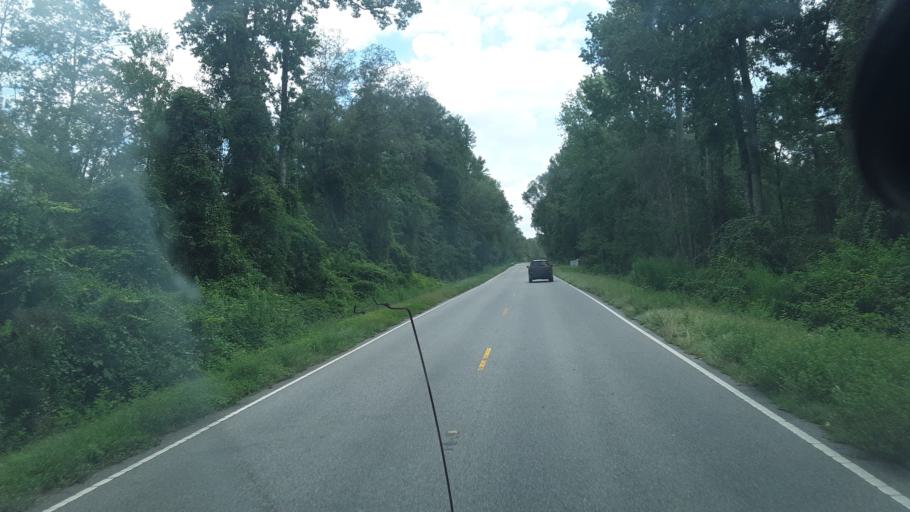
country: US
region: North Carolina
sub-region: Robeson County
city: Fairmont
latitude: 34.3447
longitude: -79.0705
